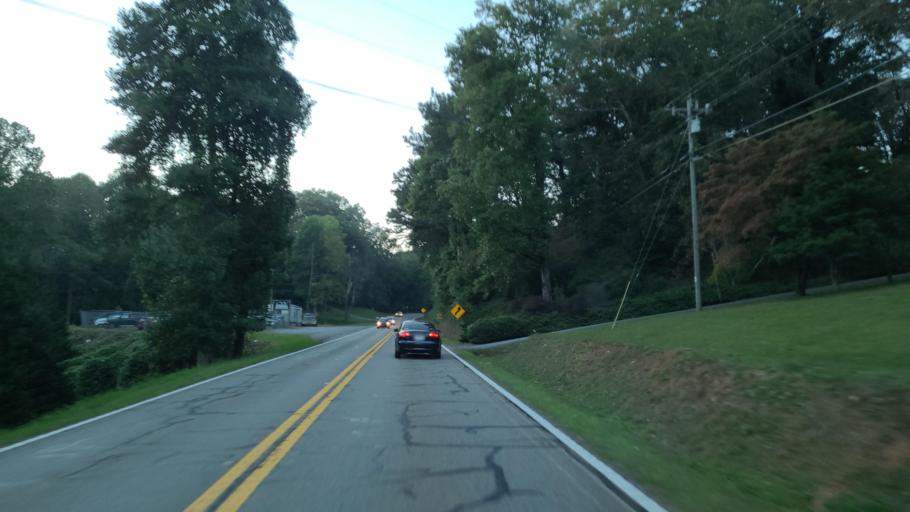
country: US
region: Georgia
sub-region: Gilmer County
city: Ellijay
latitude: 34.7137
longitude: -84.5003
